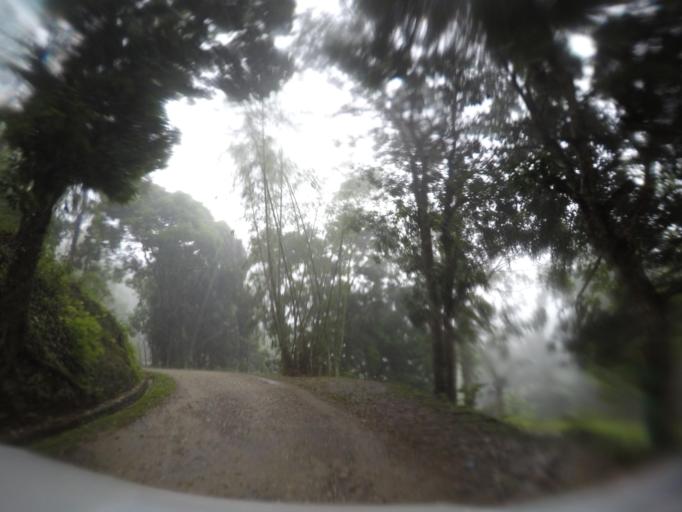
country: TL
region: Baucau
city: Venilale
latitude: -8.6416
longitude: 126.4039
